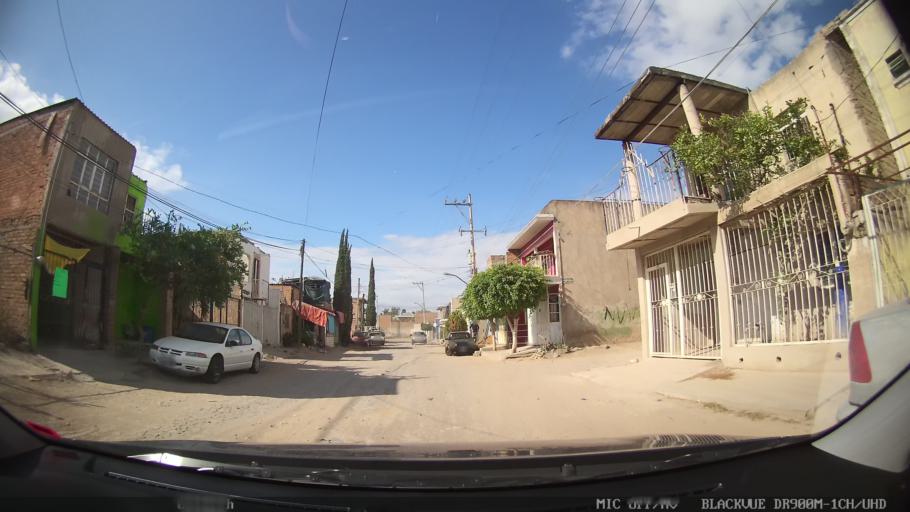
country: MX
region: Jalisco
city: Tonala
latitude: 20.6559
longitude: -103.2496
